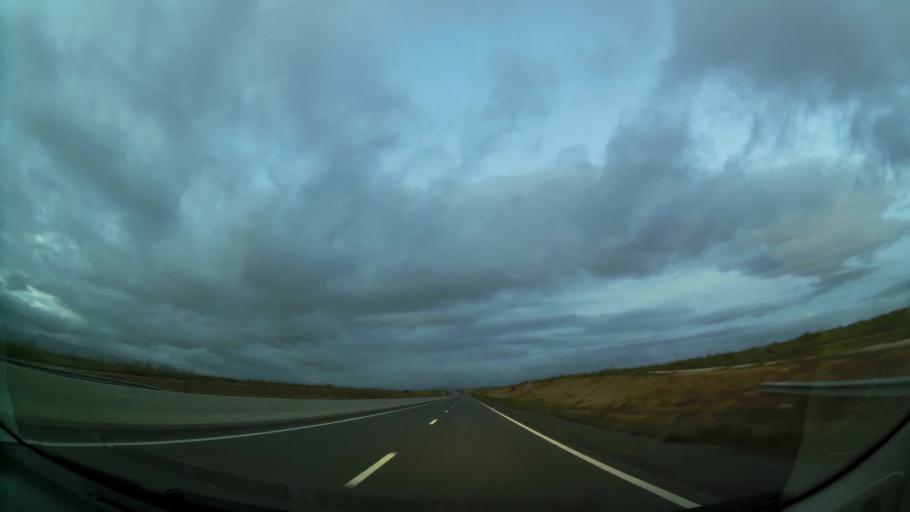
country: MA
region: Oriental
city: El Aioun
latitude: 34.6286
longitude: -2.3638
